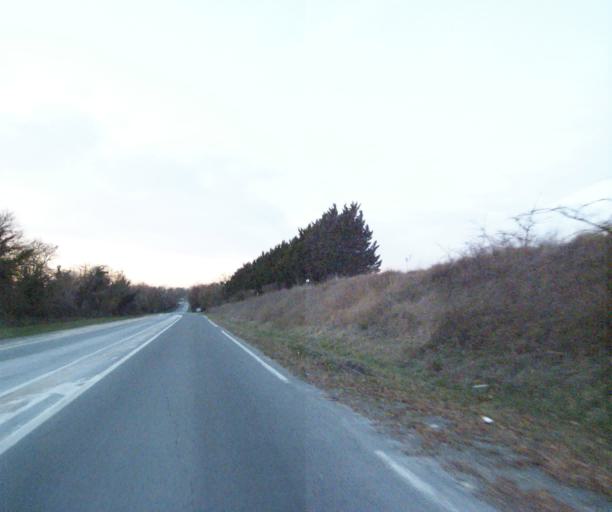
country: FR
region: Poitou-Charentes
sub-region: Departement de la Charente-Maritime
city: Saint-Porchaire
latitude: 45.8127
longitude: -0.7679
